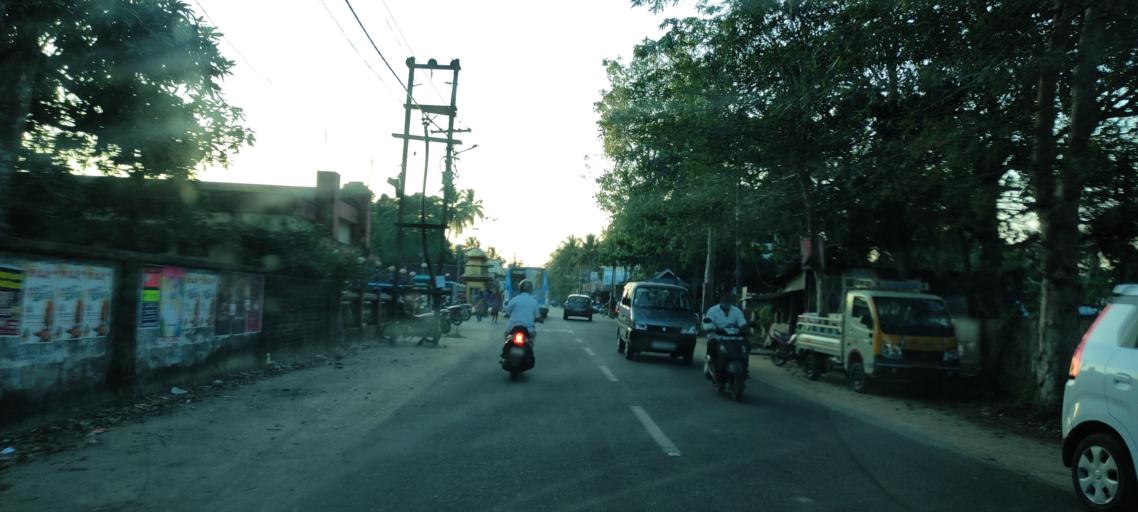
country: IN
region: Kerala
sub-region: Alappuzha
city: Kayankulam
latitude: 9.2593
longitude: 76.4385
